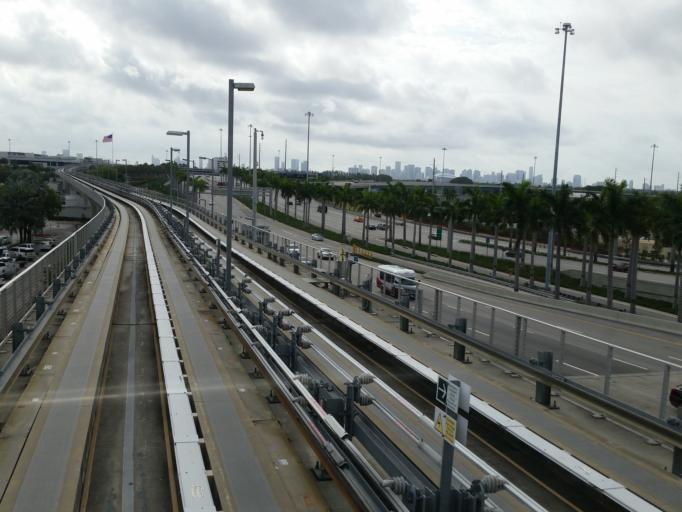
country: US
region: Florida
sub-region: Miami-Dade County
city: Miami Springs
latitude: 25.7950
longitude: -80.2702
